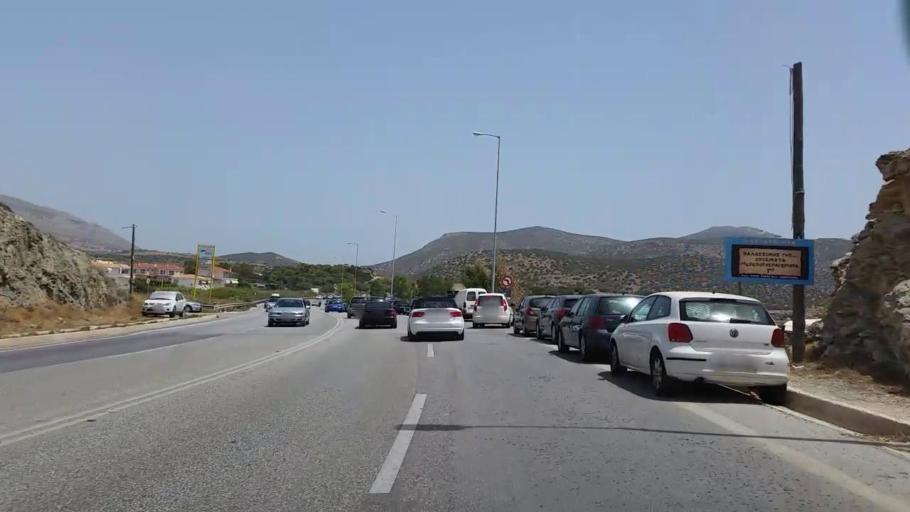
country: GR
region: Attica
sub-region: Nomarchia Anatolikis Attikis
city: Saronida
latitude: 37.7789
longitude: 23.8941
